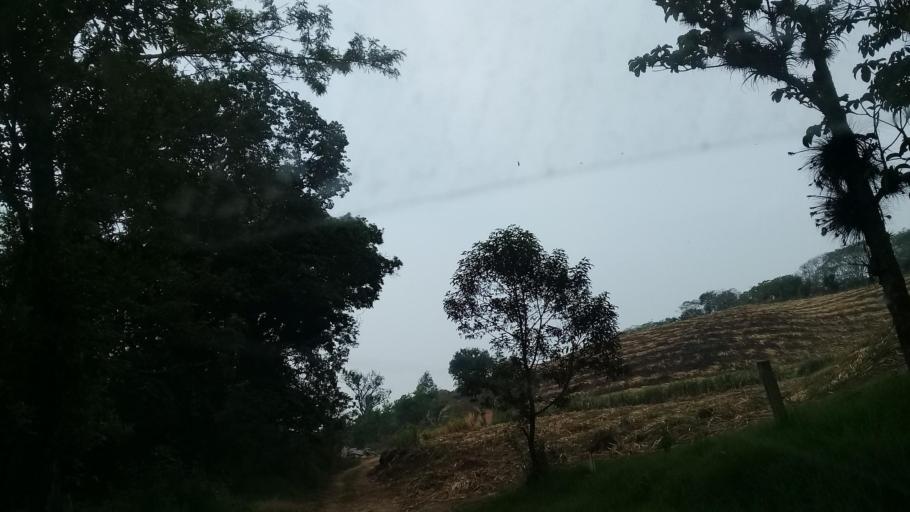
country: MX
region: Veracruz
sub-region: Xalapa
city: Fraccionamiento las Fuentes
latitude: 19.4920
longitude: -96.8996
